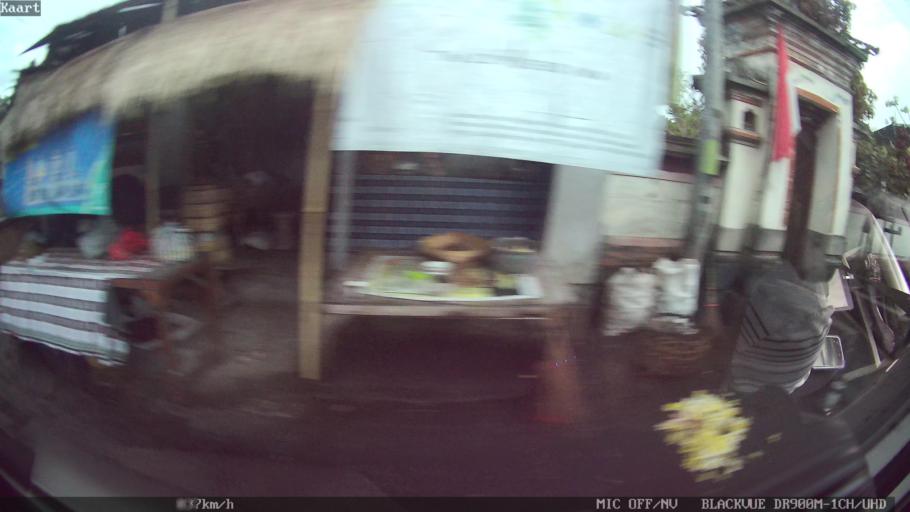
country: ID
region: Bali
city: Banjar Tebongkang
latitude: -8.5259
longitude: 115.2372
